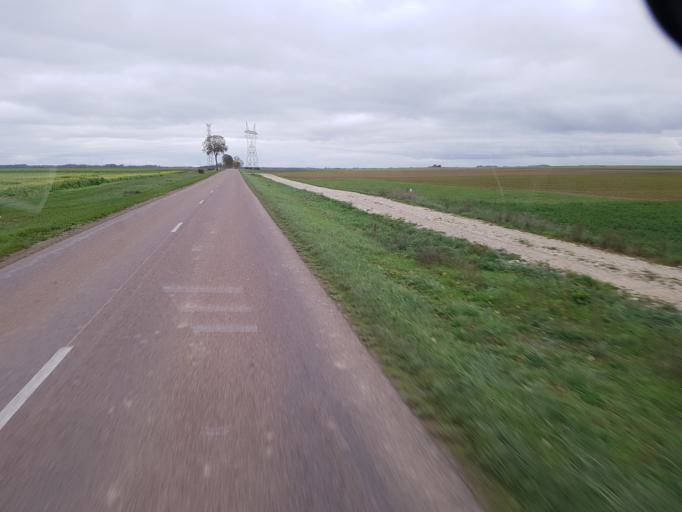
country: FR
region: Champagne-Ardenne
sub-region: Departement de l'Aube
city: Mery-sur-Seine
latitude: 48.5282
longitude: 3.8667
